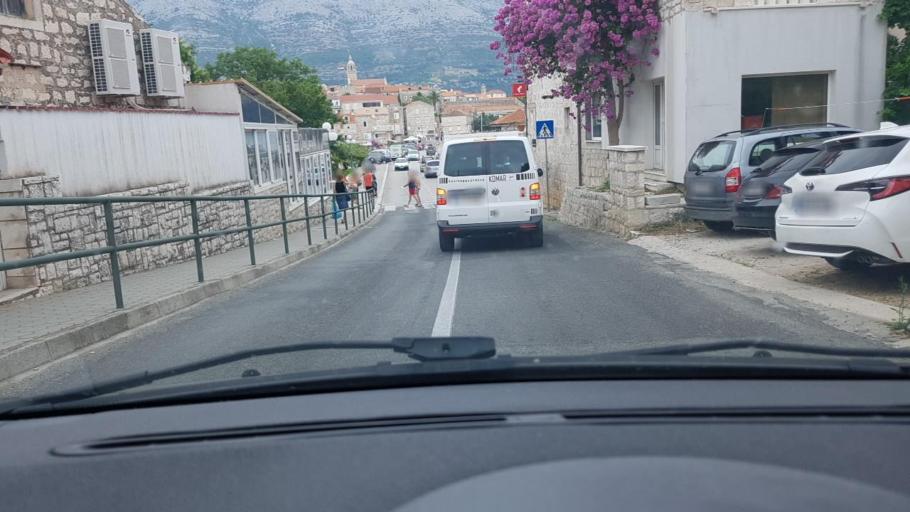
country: HR
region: Dubrovacko-Neretvanska
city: Korcula
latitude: 42.9583
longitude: 17.1347
